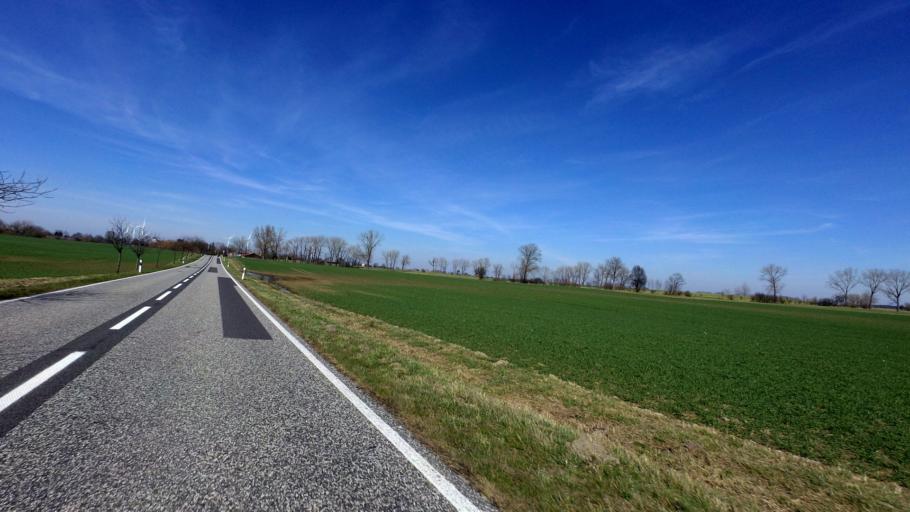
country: DE
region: Brandenburg
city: Furstenwalde
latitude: 52.4237
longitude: 14.0461
